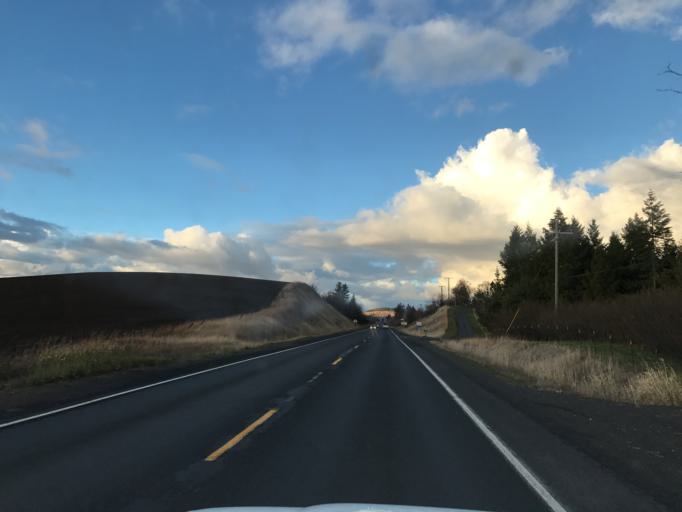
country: US
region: Idaho
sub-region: Latah County
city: Moscow
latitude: 46.7524
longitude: -117.0016
